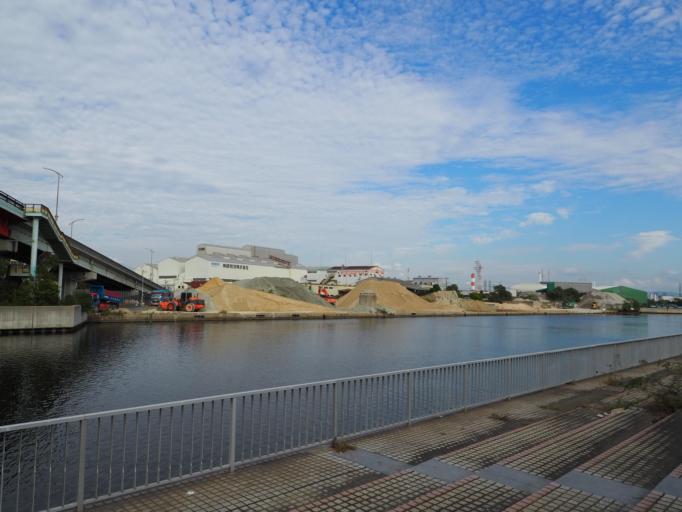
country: JP
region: Hyogo
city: Amagasaki
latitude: 34.7016
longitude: 135.3931
